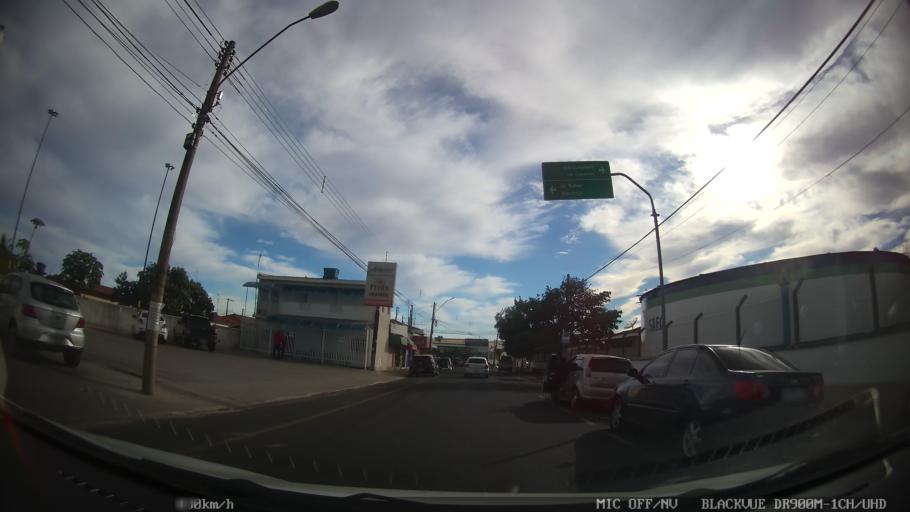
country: BR
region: Sao Paulo
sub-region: Catanduva
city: Catanduva
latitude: -21.1219
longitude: -48.9669
